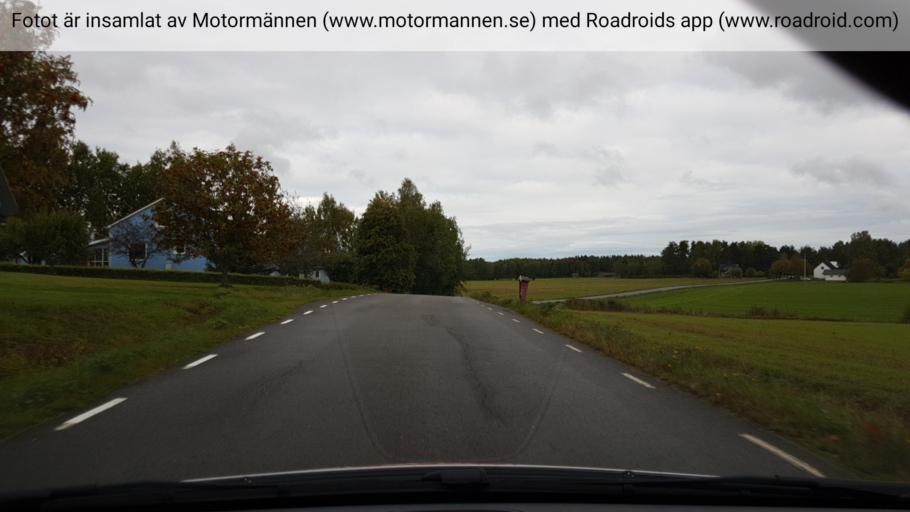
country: SE
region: Vaermland
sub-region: Saffle Kommun
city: Saeffle
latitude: 59.1369
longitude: 13.0991
